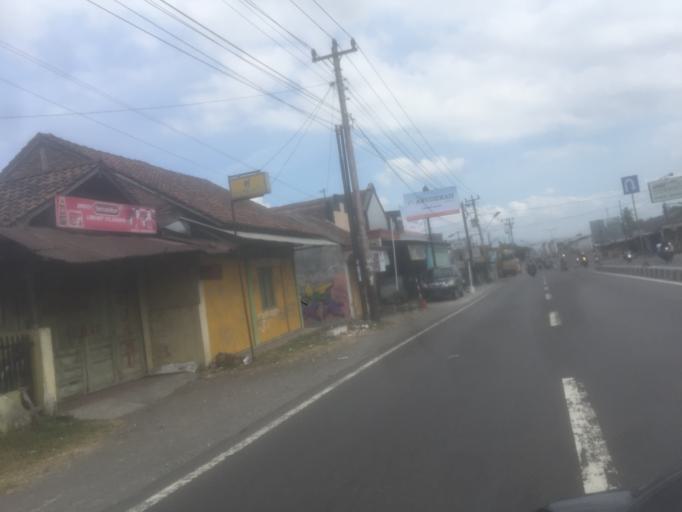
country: ID
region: Central Java
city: Muntilan
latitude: -7.6078
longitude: 110.3027
